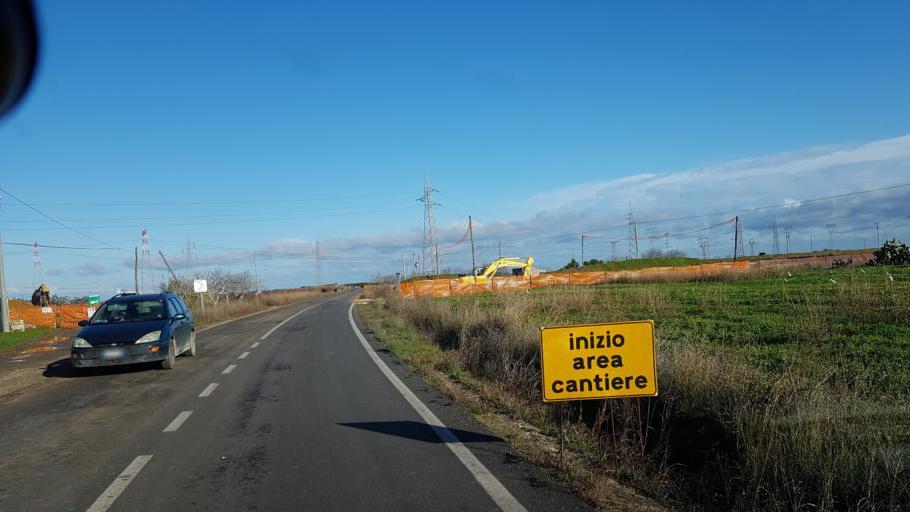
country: IT
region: Apulia
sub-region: Provincia di Brindisi
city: Tuturano
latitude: 40.5522
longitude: 17.9468
